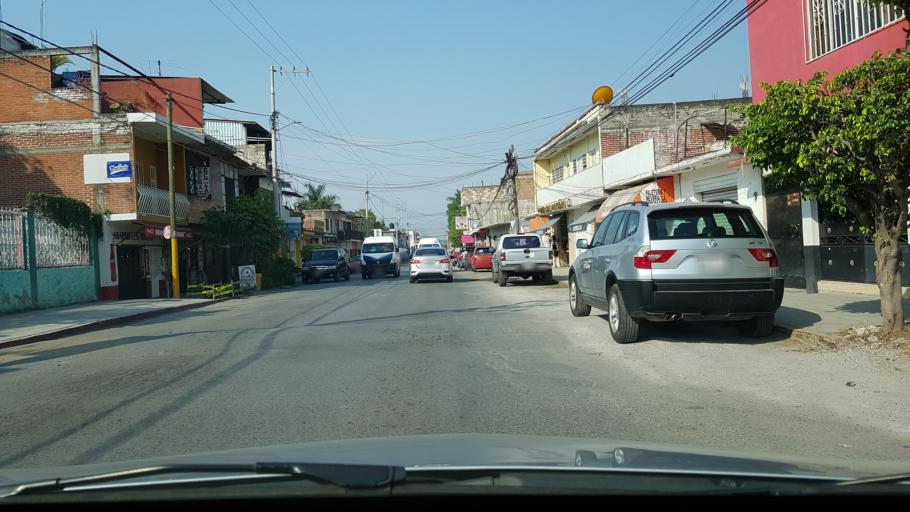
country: MX
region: Morelos
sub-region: Jojutla
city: Jojutla
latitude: 18.6194
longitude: -99.1735
